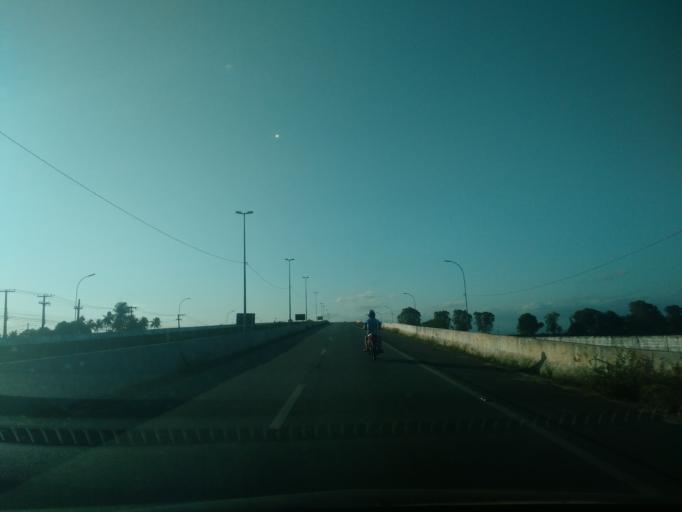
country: BR
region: Alagoas
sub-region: Satuba
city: Satuba
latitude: -9.5157
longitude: -35.8041
